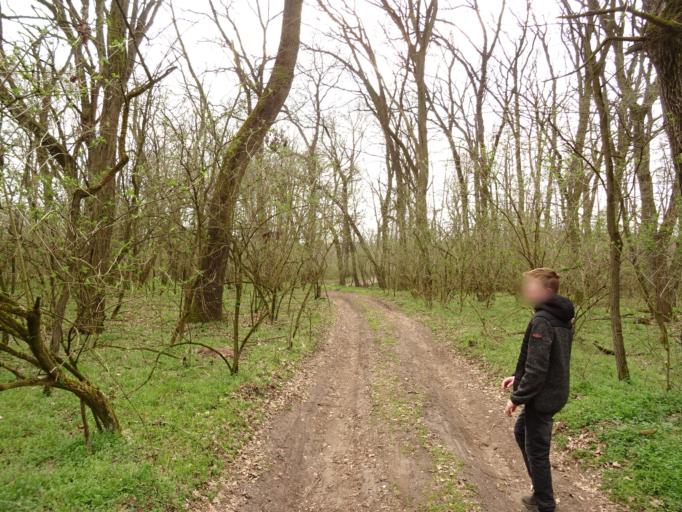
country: HU
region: Pest
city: Nagykoros
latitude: 47.0585
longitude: 19.7192
